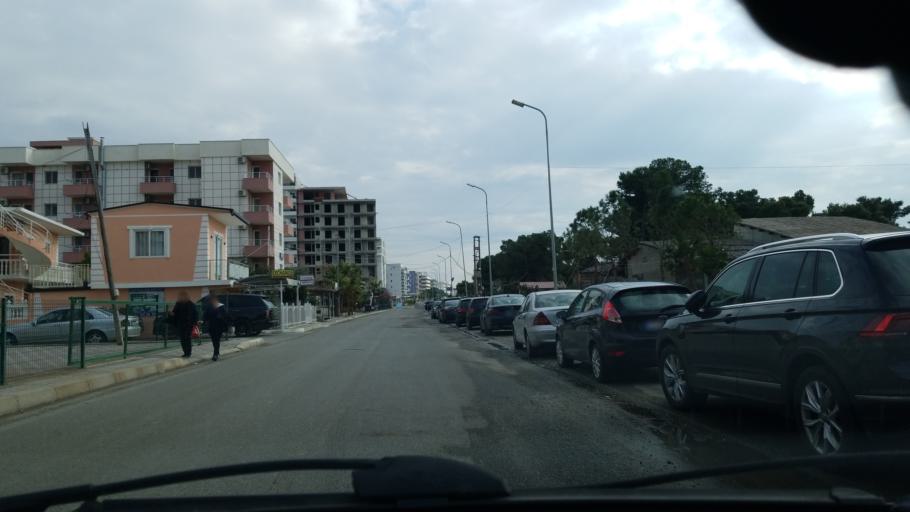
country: AL
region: Lezhe
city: Shengjin
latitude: 41.8054
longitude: 19.5999
